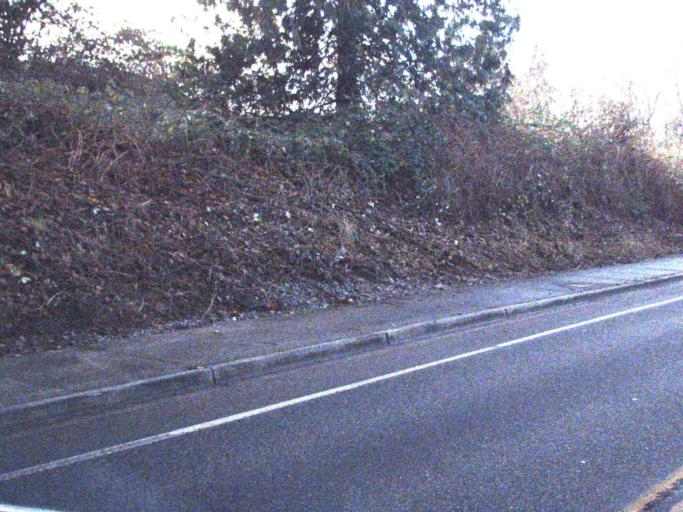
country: US
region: Washington
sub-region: Skagit County
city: Big Lake
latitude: 48.4344
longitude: -122.2779
